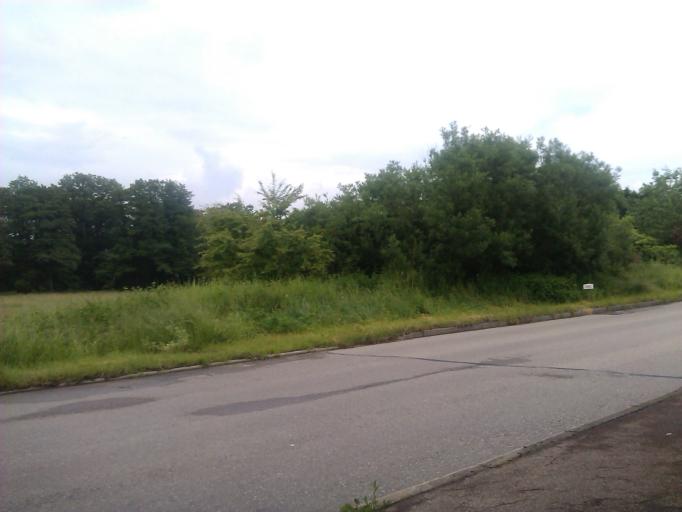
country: DE
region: Baden-Wuerttemberg
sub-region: Regierungsbezirk Stuttgart
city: Oberrot
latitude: 49.0176
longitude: 9.6607
